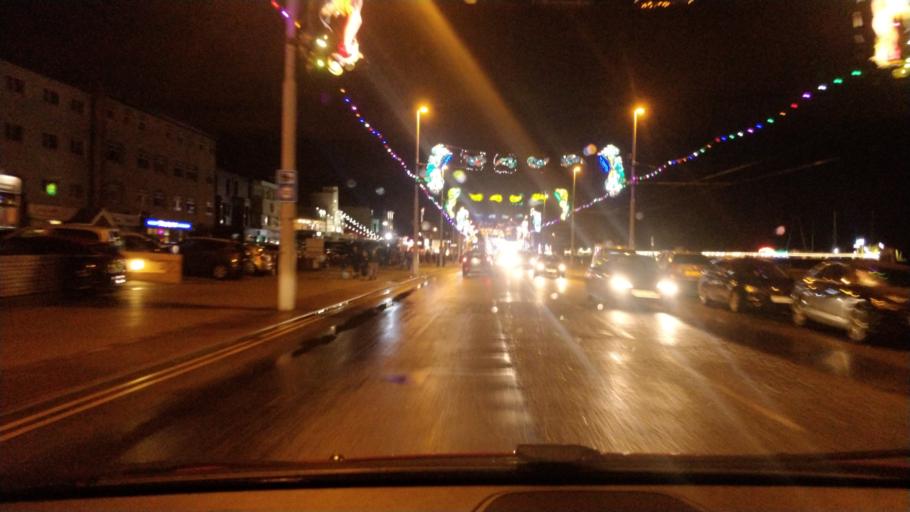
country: GB
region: England
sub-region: Blackpool
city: Blackpool
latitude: 53.8009
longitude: -3.0555
